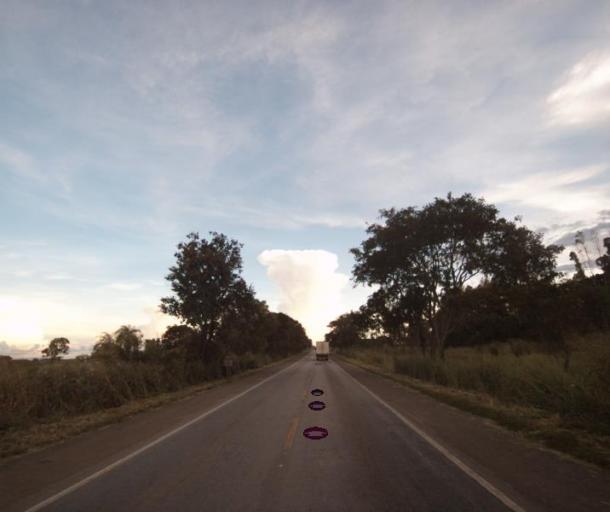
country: BR
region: Goias
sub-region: Uruacu
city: Uruacu
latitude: -14.3282
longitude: -49.1531
